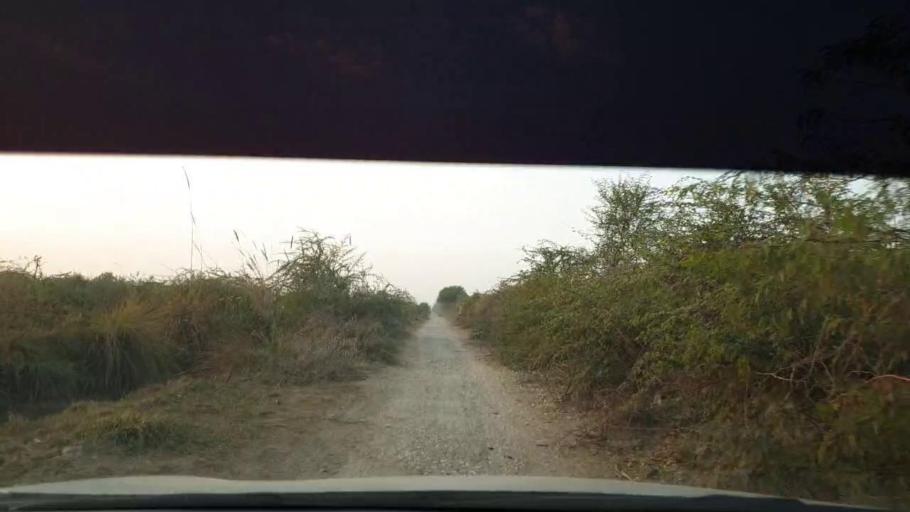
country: PK
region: Sindh
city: Berani
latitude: 25.7696
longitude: 68.9803
